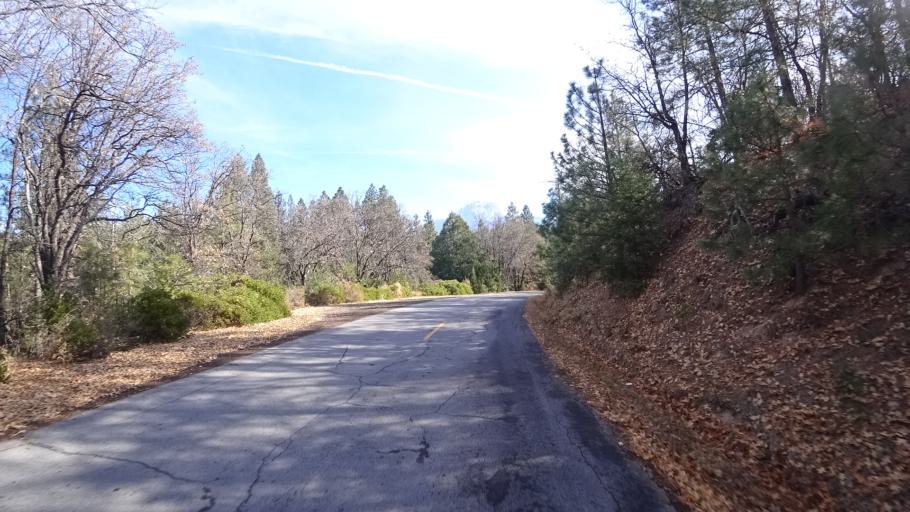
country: US
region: California
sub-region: Siskiyou County
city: Weed
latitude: 41.4323
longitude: -122.4153
